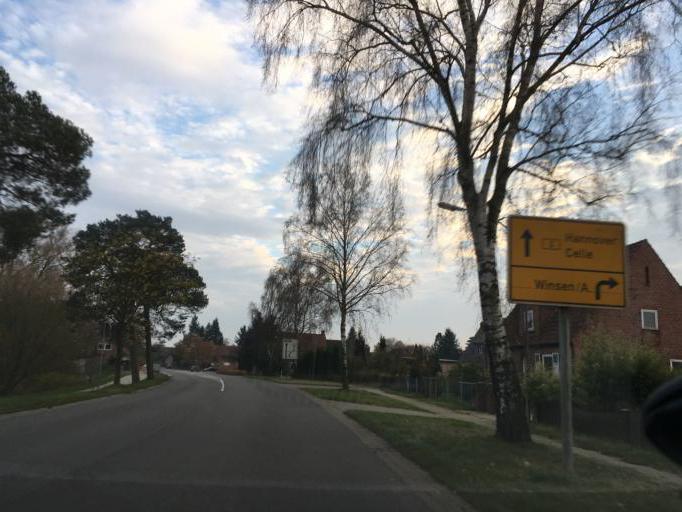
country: DE
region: Lower Saxony
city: Hambuhren
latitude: 52.6984
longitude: 9.9814
